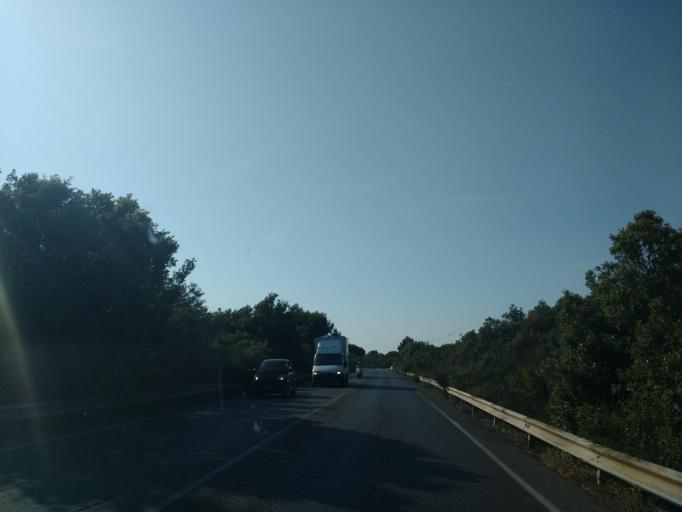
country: IT
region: Latium
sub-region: Citta metropolitana di Roma Capitale
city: Acilia-Castel Fusano-Ostia Antica
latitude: 41.6929
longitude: 12.3661
